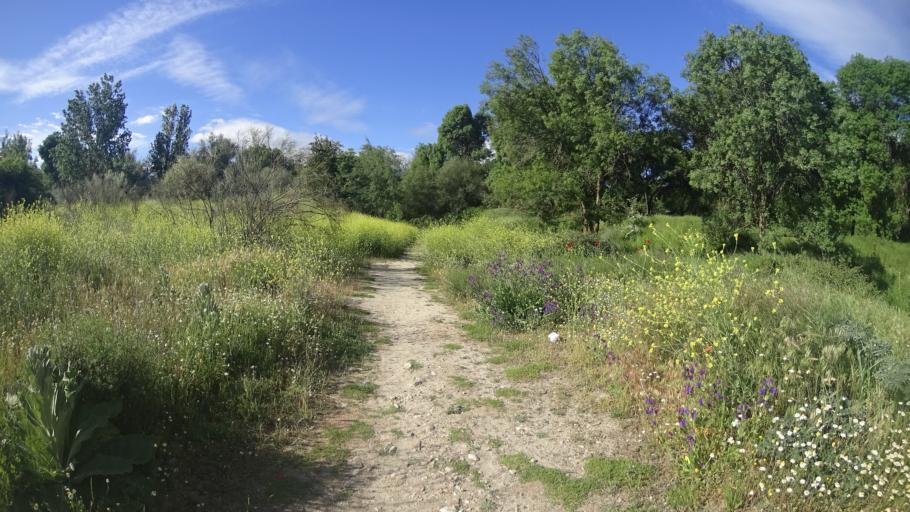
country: ES
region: Madrid
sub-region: Provincia de Madrid
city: Villanueva del Pardillo
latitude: 40.5130
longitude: -3.9390
